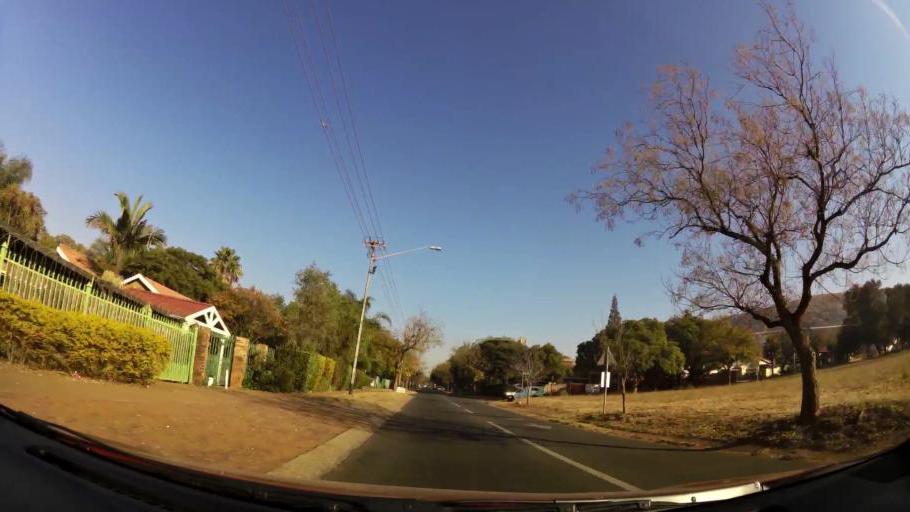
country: ZA
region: Gauteng
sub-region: City of Tshwane Metropolitan Municipality
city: Pretoria
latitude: -25.6981
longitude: 28.1618
